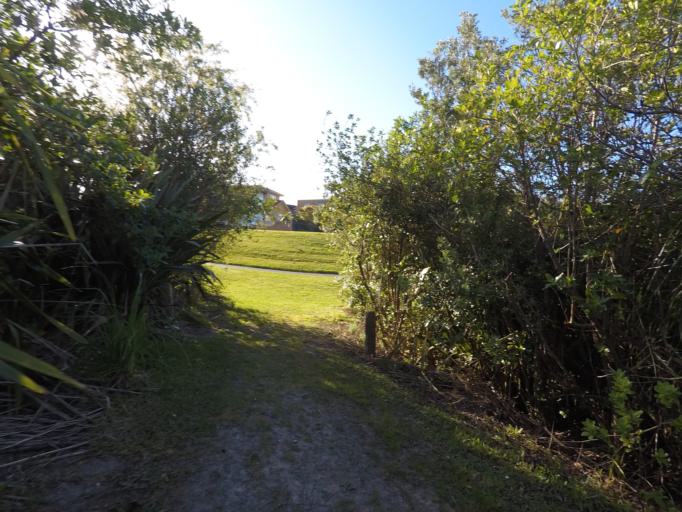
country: NZ
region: Auckland
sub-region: Auckland
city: Rosebank
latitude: -36.8377
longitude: 174.6613
